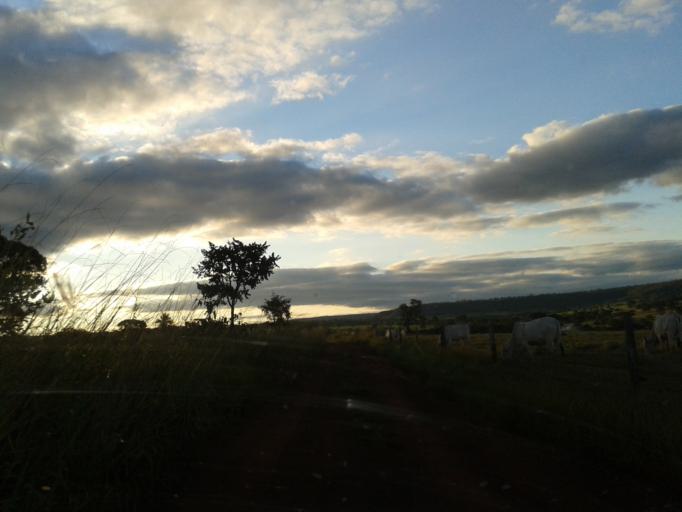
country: BR
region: Minas Gerais
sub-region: Campina Verde
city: Campina Verde
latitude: -19.5071
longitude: -49.6812
